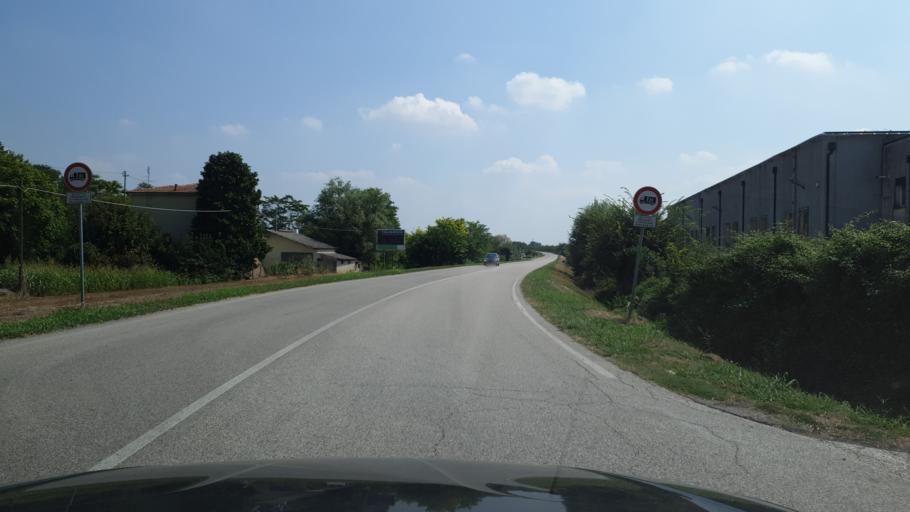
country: IT
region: Veneto
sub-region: Provincia di Rovigo
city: Villamarzana
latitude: 45.0190
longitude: 11.6827
